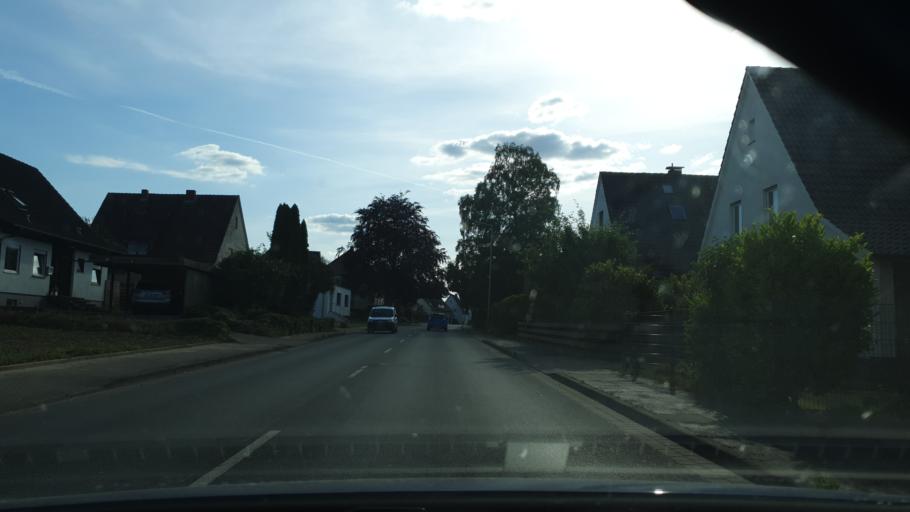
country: DE
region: North Rhine-Westphalia
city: Spenge
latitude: 52.1410
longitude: 8.5127
